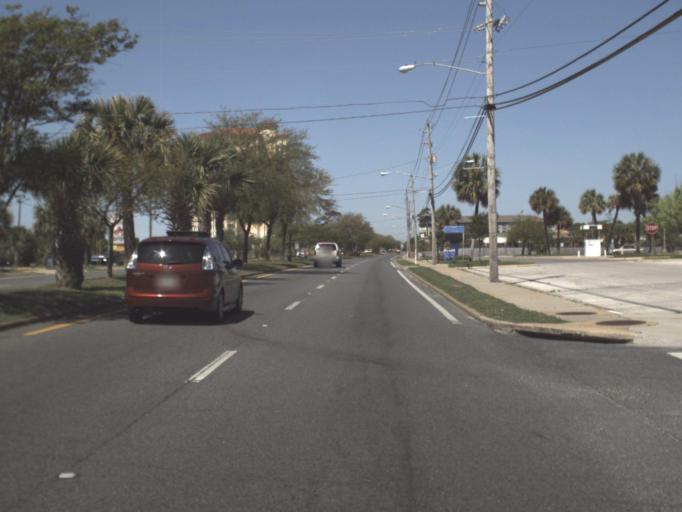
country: US
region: Florida
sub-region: Okaloosa County
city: Fort Walton Beach
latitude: 30.4047
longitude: -86.6191
